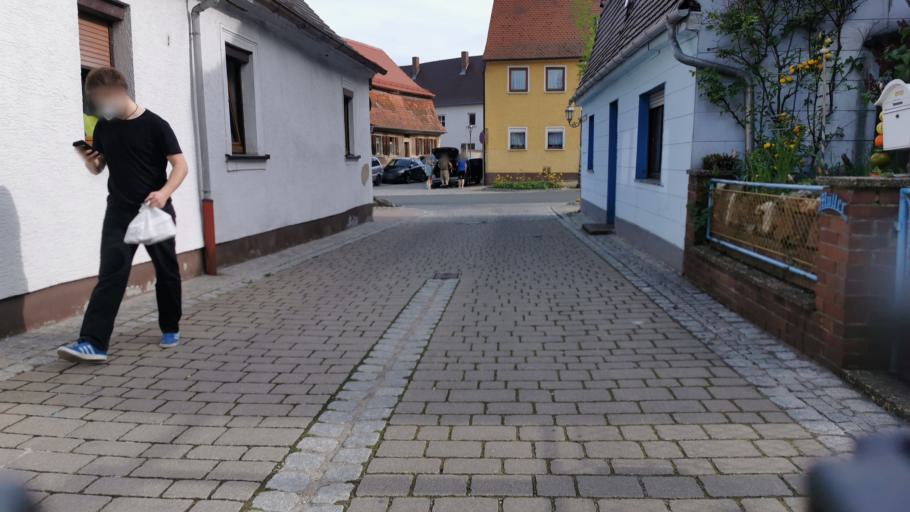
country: DE
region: Bavaria
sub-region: Regierungsbezirk Mittelfranken
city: Hochstadt an der Aisch
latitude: 49.7031
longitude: 10.8081
